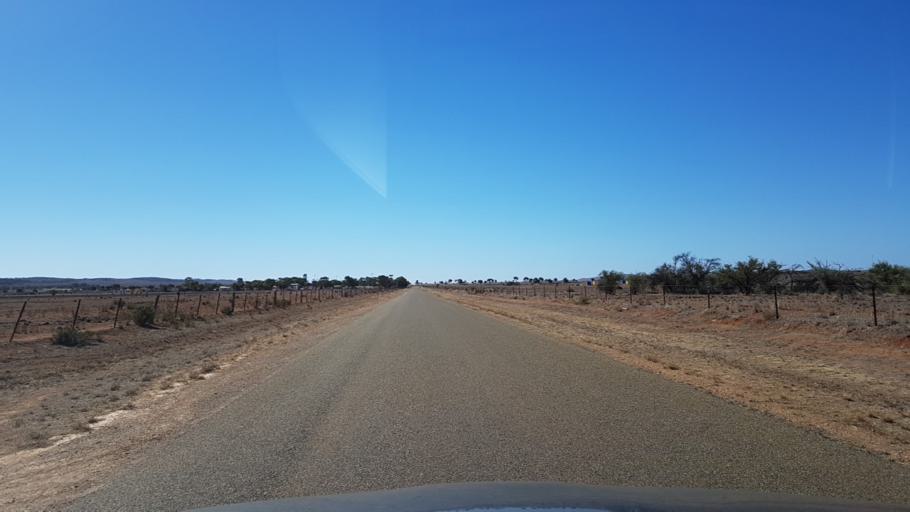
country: AU
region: South Australia
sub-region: Peterborough
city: Peterborough
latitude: -32.9802
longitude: 138.8521
